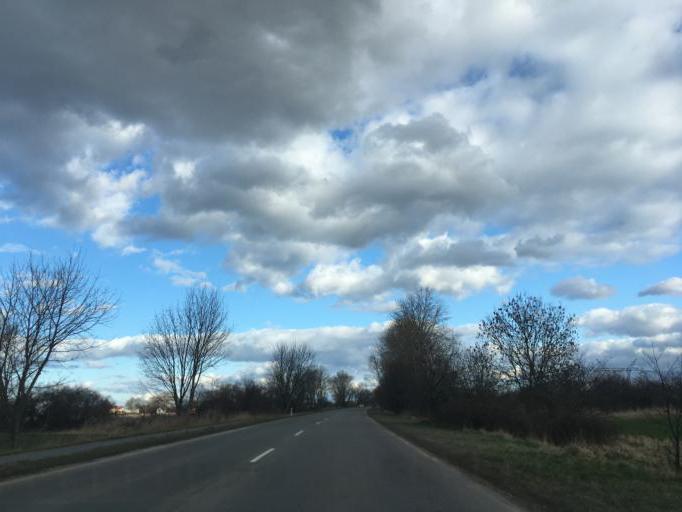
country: PL
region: Pomeranian Voivodeship
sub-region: Powiat gdanski
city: Cedry Wielkie
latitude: 54.3295
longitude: 18.7729
